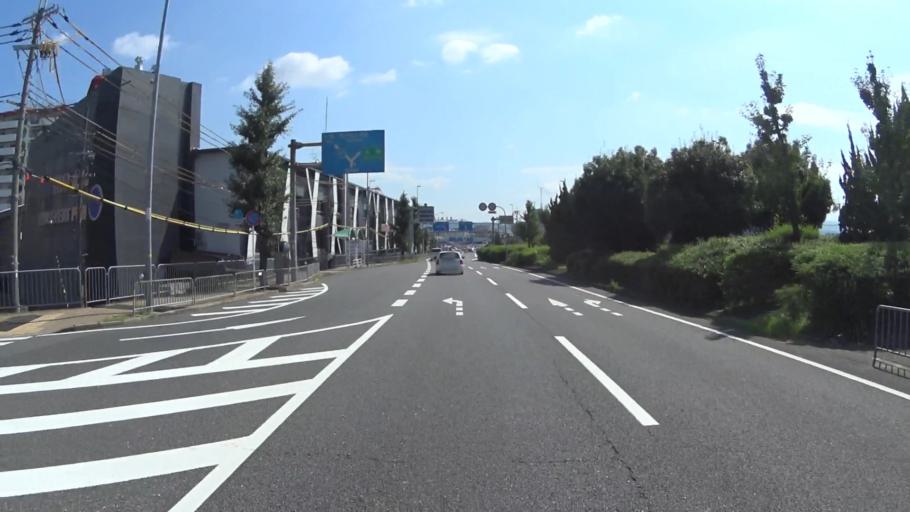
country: JP
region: Kyoto
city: Muko
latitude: 34.9740
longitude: 135.7267
